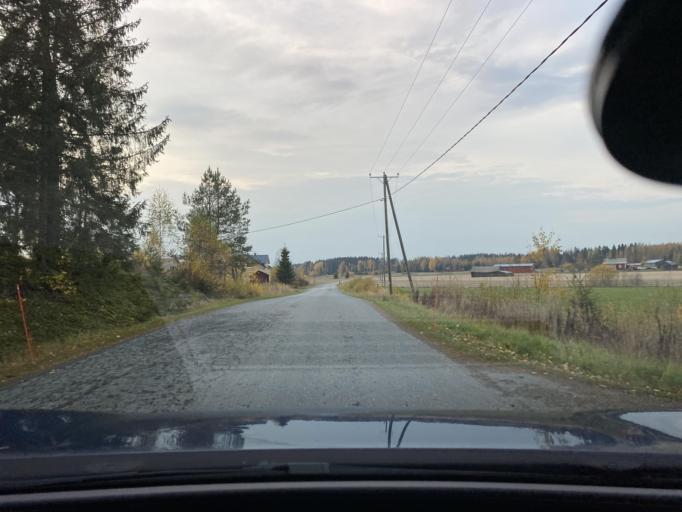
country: FI
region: Pirkanmaa
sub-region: Lounais-Pirkanmaa
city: Punkalaidun
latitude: 61.0761
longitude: 22.9646
